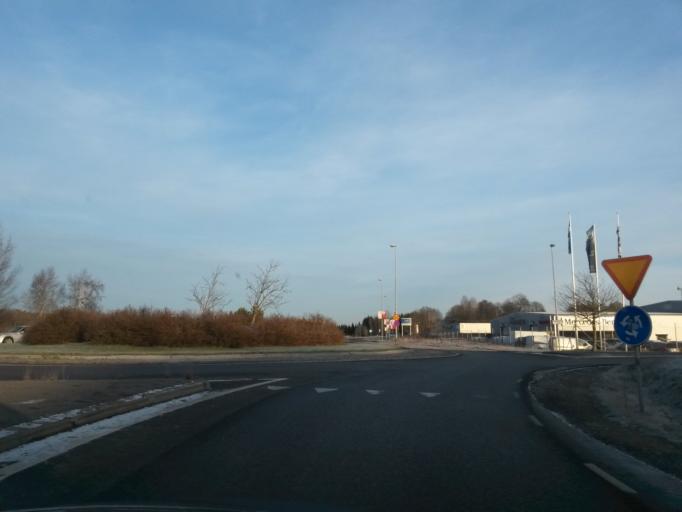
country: SE
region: Vaestra Goetaland
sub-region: Trollhattan
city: Trollhattan
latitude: 58.3171
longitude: 12.3086
